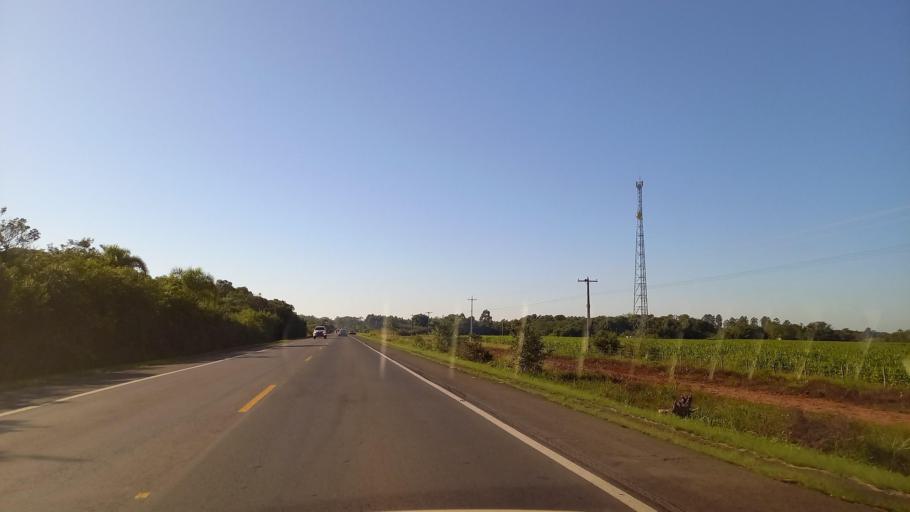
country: BR
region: Rio Grande do Sul
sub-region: Venancio Aires
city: Venancio Aires
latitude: -29.6668
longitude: -52.0477
